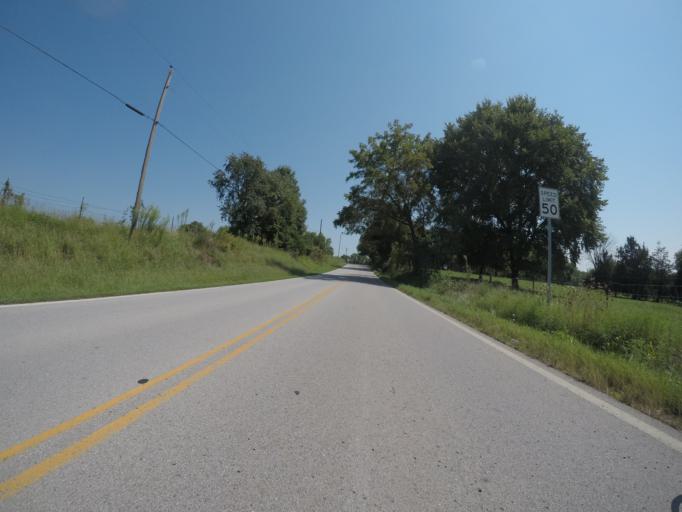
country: US
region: Kansas
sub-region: Leavenworth County
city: Lansing
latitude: 39.2459
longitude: -94.8734
